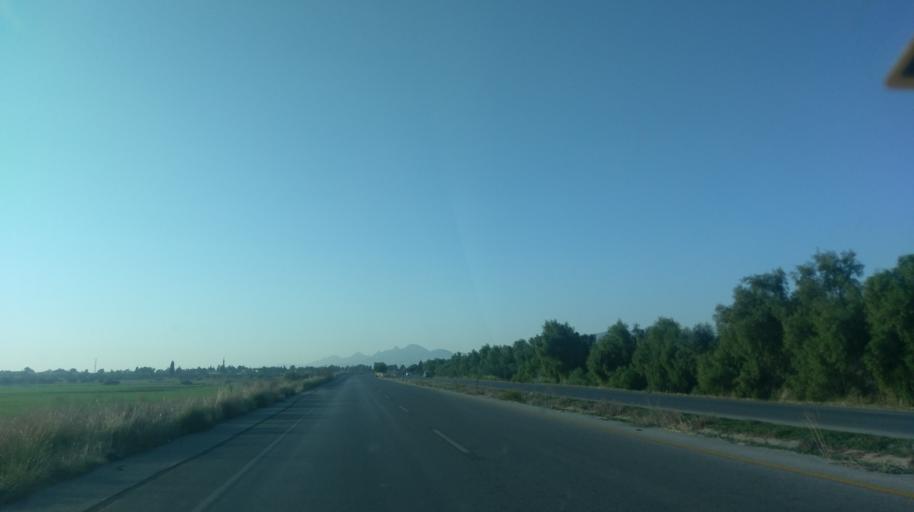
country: CY
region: Ammochostos
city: Lefkonoiko
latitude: 35.2017
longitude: 33.6030
